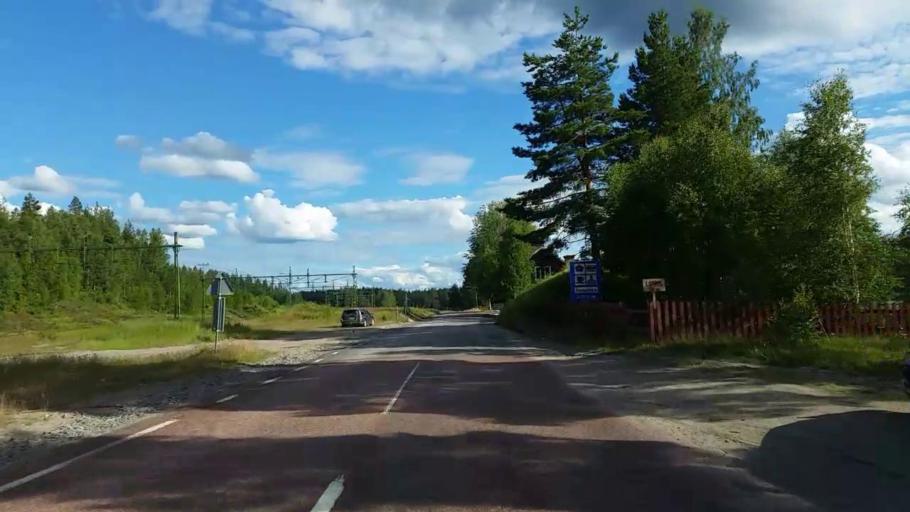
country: SE
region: Gaevleborg
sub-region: Ljusdals Kommun
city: Farila
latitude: 62.0226
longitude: 15.9011
